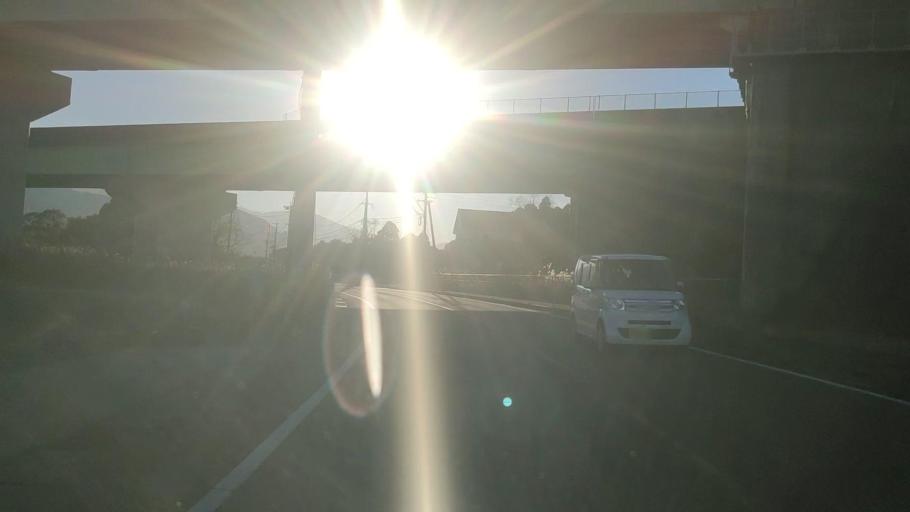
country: JP
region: Miyazaki
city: Miyazaki-shi
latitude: 31.8527
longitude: 131.3575
